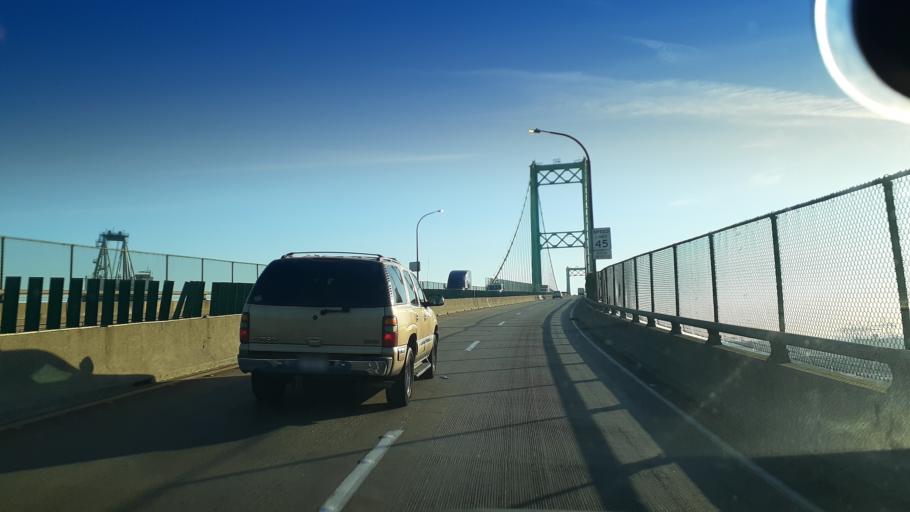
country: US
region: California
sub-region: Los Angeles County
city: San Pedro
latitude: 33.7503
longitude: -118.2772
